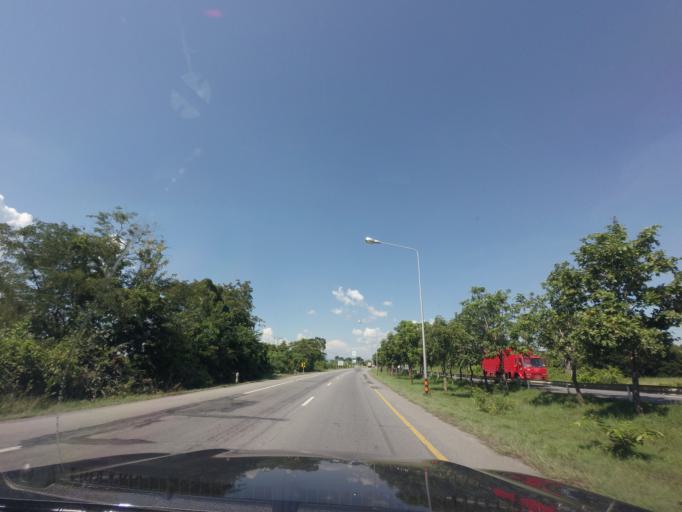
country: TH
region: Nakhon Ratchasima
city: Non Sung
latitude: 15.2204
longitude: 102.3612
